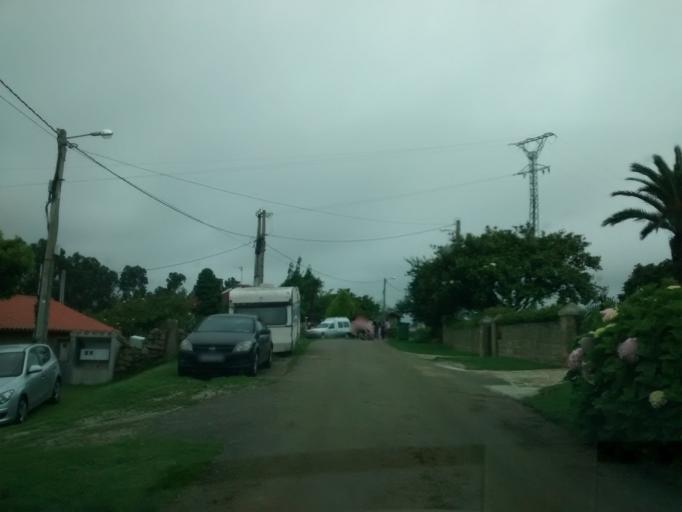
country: ES
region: Asturias
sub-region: Province of Asturias
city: Villaviciosa
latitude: 43.5466
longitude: -5.4040
